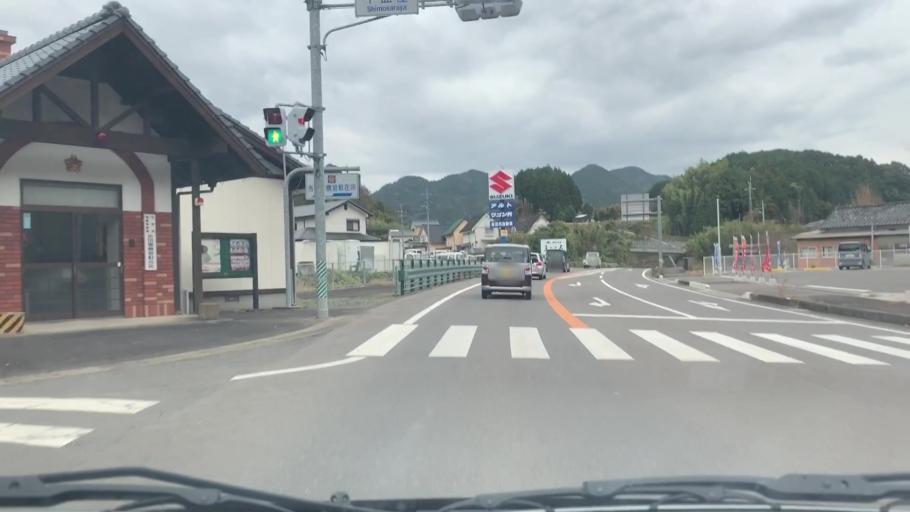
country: JP
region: Saga Prefecture
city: Ureshinomachi-shimojuku
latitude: 33.0885
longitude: 130.0136
